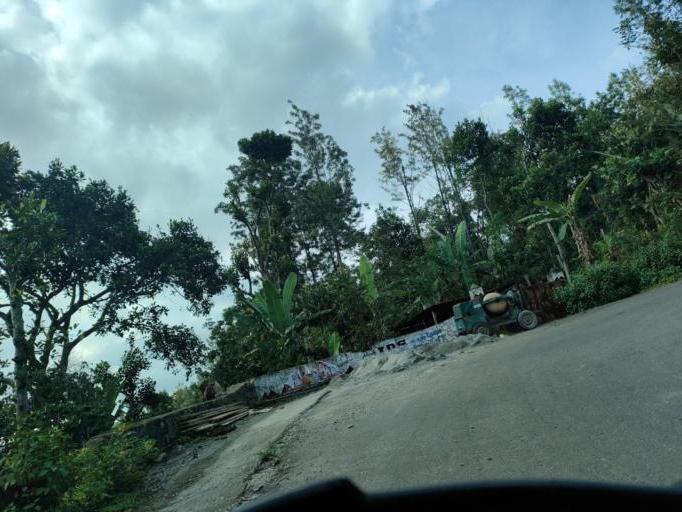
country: IN
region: Tamil Nadu
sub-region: Dindigul
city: Kodaikanal
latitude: 10.2781
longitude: 77.5316
